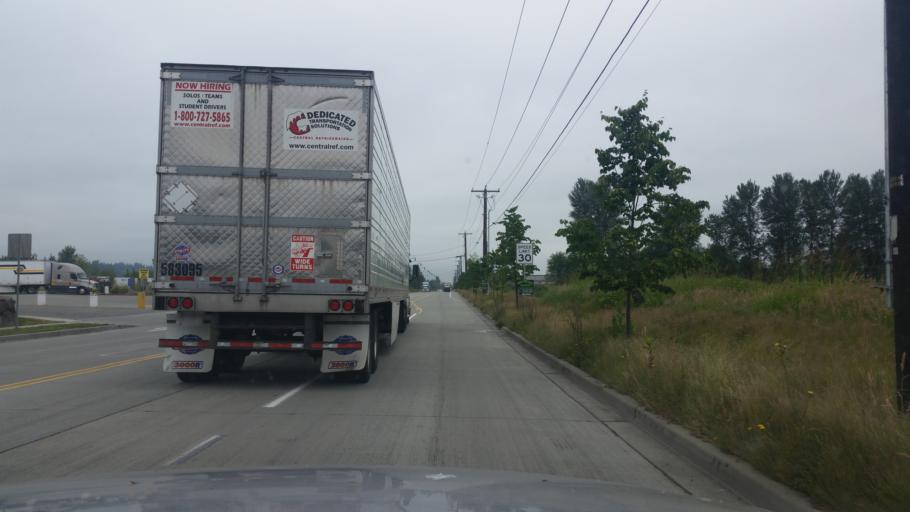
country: US
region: Washington
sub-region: King County
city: Pacific
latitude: 47.2361
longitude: -122.2487
